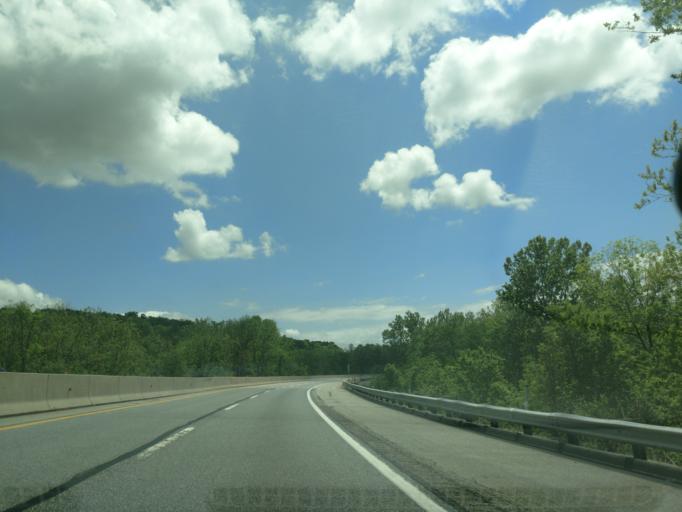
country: US
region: Pennsylvania
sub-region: Lancaster County
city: Denver
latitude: 40.2385
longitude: -76.1314
